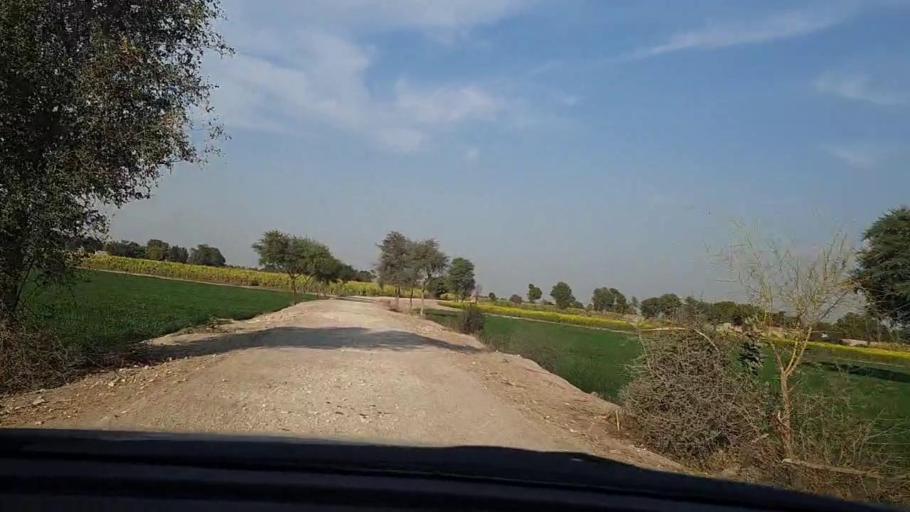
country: PK
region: Sindh
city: Daulatpur
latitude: 26.3299
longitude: 68.0275
